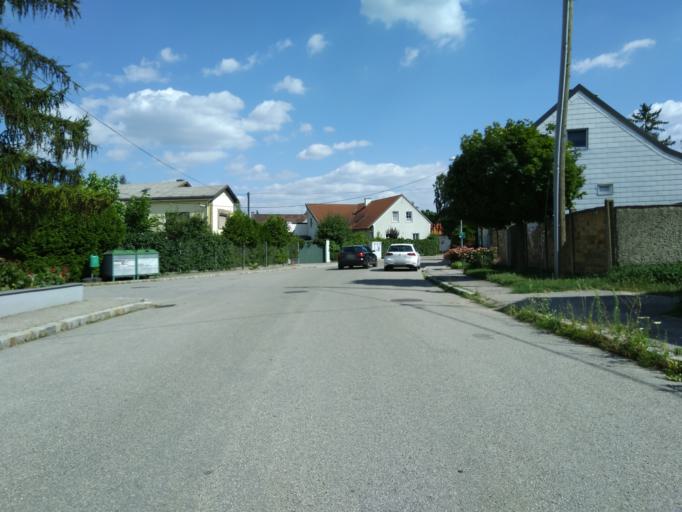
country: AT
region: Lower Austria
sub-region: Politischer Bezirk Mistelbach
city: Pillichsdorf
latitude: 48.3651
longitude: 16.5332
